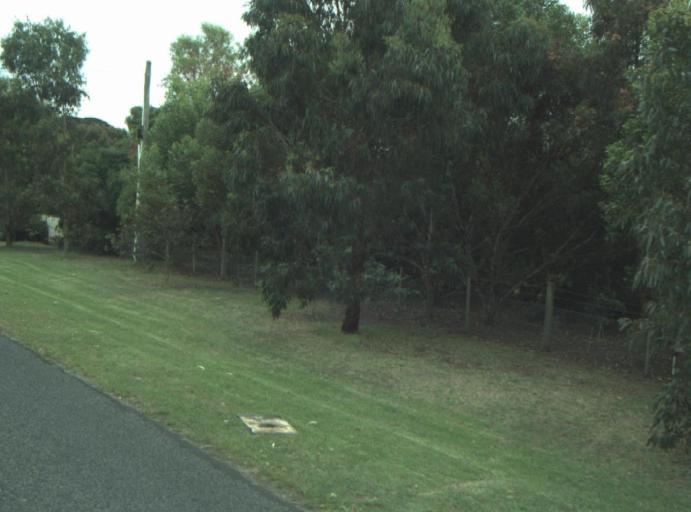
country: AU
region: Victoria
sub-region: Greater Geelong
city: Leopold
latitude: -38.2205
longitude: 144.4592
